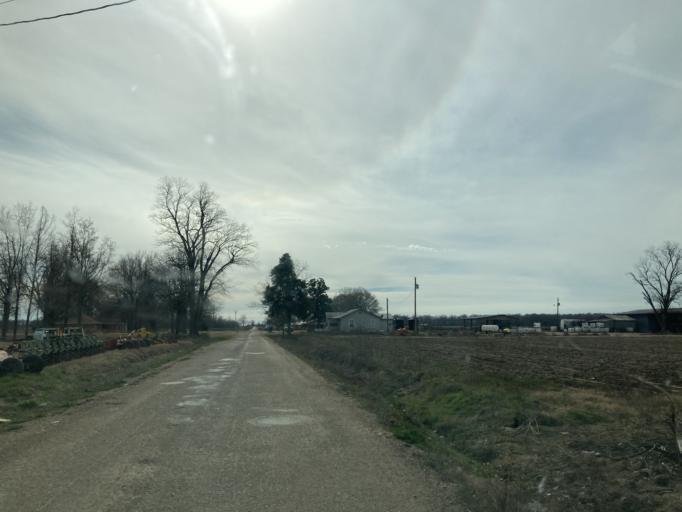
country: US
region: Mississippi
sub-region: Humphreys County
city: Belzoni
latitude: 33.1378
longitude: -90.5895
